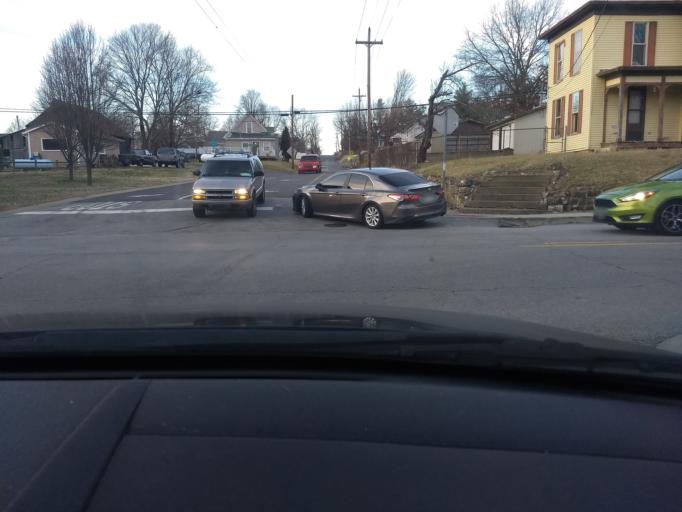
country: US
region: Indiana
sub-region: Floyd County
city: Georgetown
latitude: 38.2944
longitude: -85.9755
